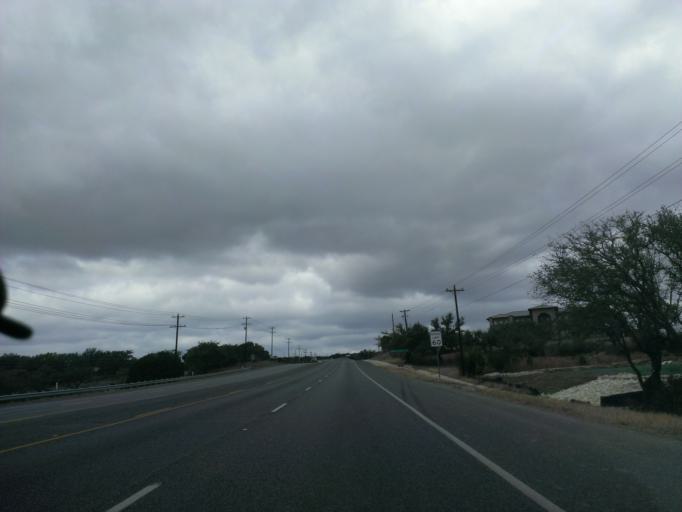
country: US
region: Texas
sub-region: Travis County
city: The Hills
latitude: 30.3423
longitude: -98.0446
